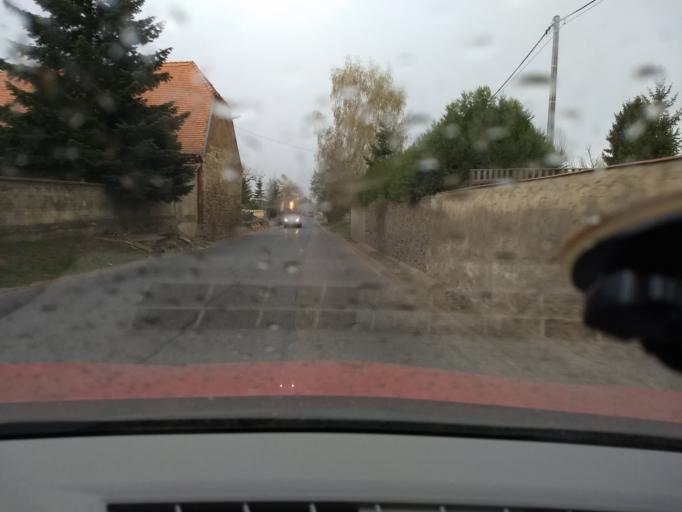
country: CZ
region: Central Bohemia
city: Rudna
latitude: 50.0400
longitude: 14.1884
